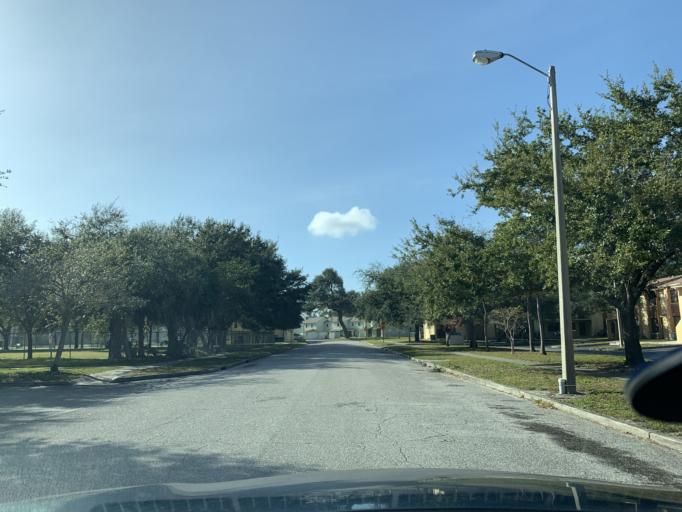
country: US
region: Florida
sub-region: Pinellas County
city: Saint Petersburg
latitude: 27.7752
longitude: -82.6485
